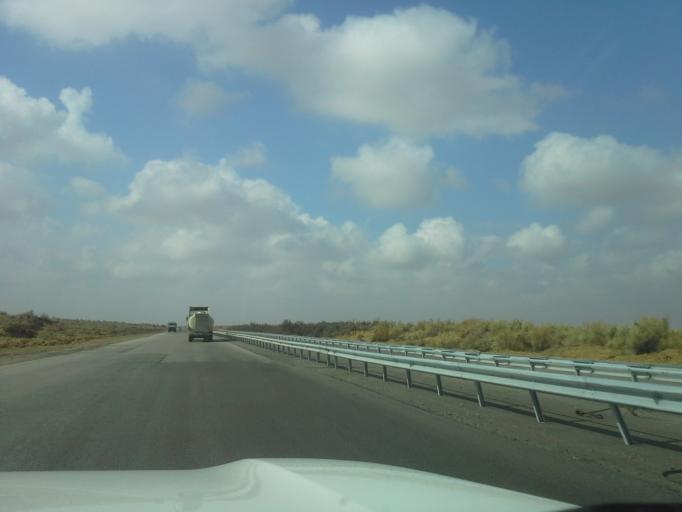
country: TM
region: Mary
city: Mary
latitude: 37.3763
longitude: 61.4700
